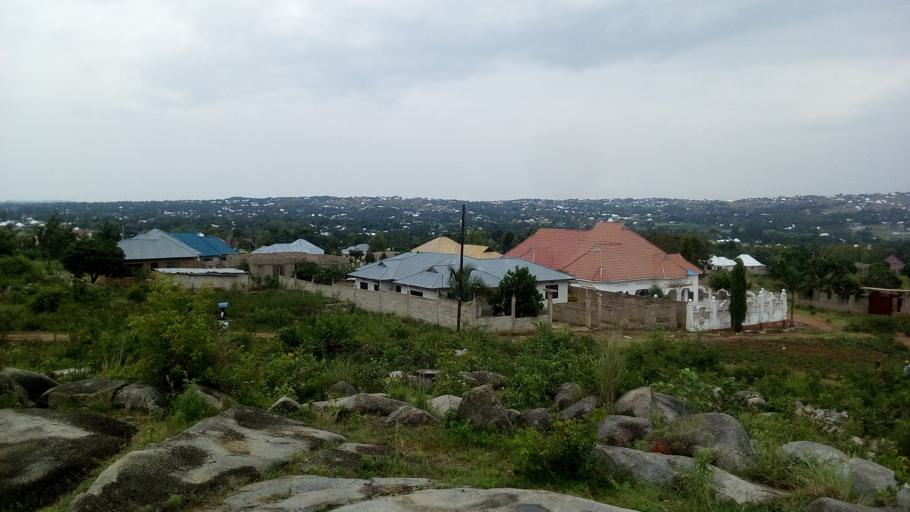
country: TZ
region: Mwanza
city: Mwanza
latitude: -2.4936
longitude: 32.9710
